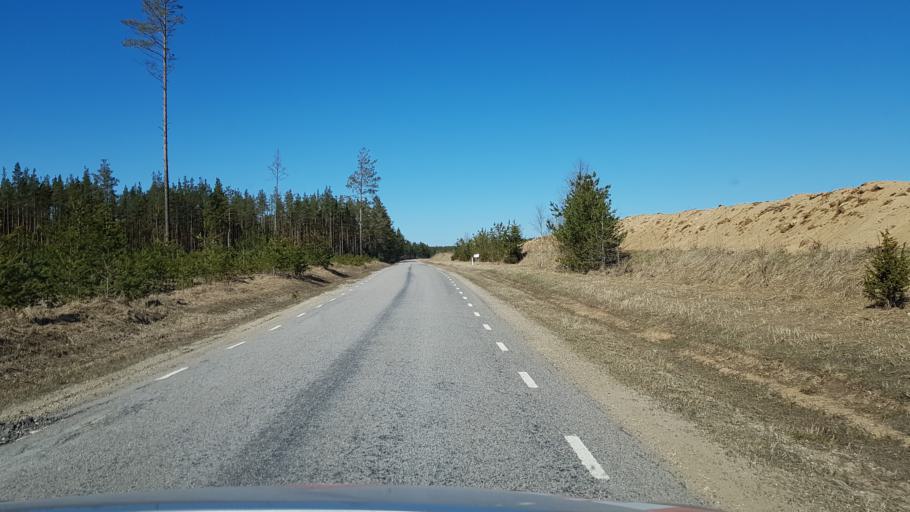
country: EE
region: Laeaene-Virumaa
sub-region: Viru-Nigula vald
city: Kunda
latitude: 59.5035
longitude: 26.4788
